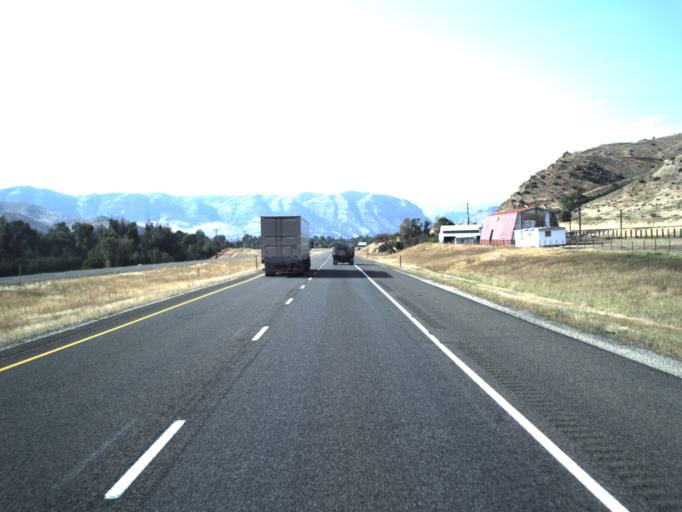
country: US
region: Utah
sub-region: Summit County
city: Coalville
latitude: 40.9917
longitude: -111.4579
